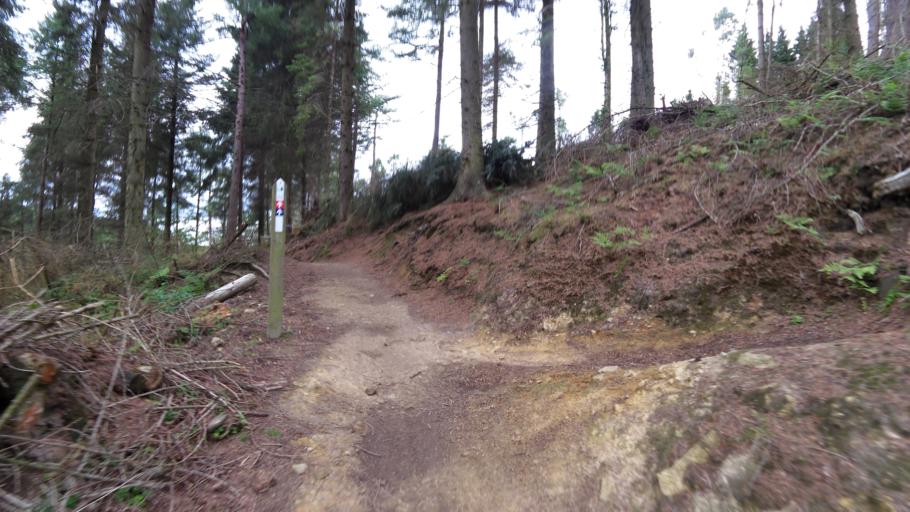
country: GB
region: England
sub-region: North Yorkshire
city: Thornton Dale
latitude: 54.2776
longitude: -0.6857
